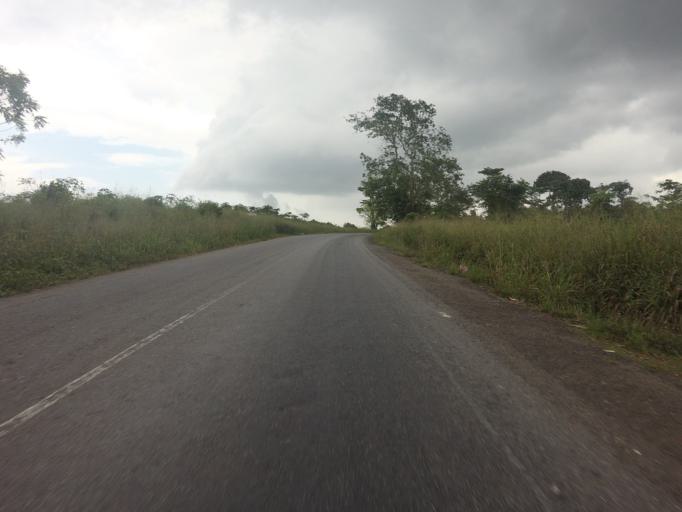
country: GH
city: Akropong
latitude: 5.9519
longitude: -0.1168
